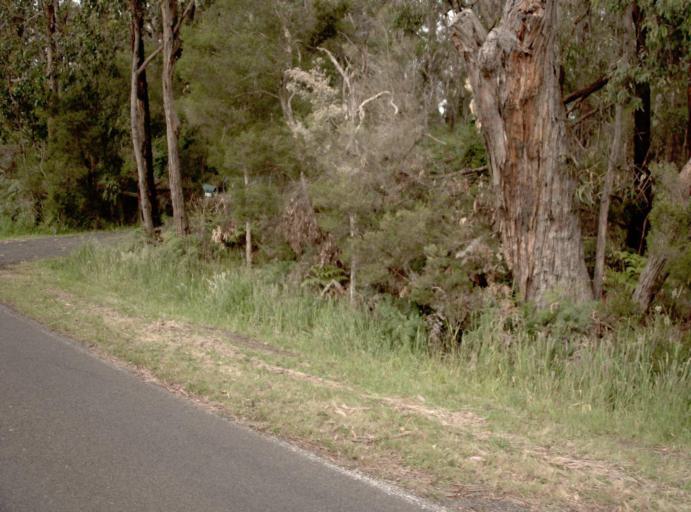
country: AU
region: Victoria
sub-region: Bass Coast
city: North Wonthaggi
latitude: -38.5322
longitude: 145.6992
